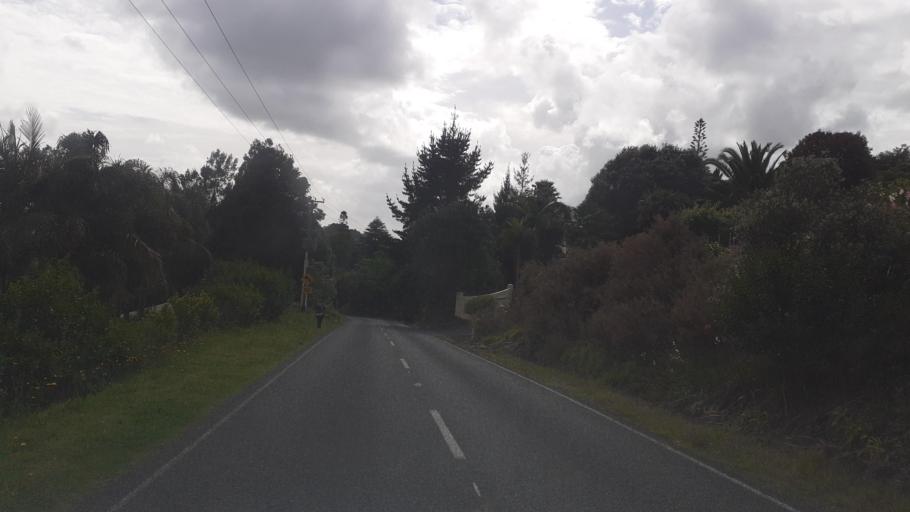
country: NZ
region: Northland
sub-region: Far North District
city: Kerikeri
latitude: -35.2173
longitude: 173.9812
